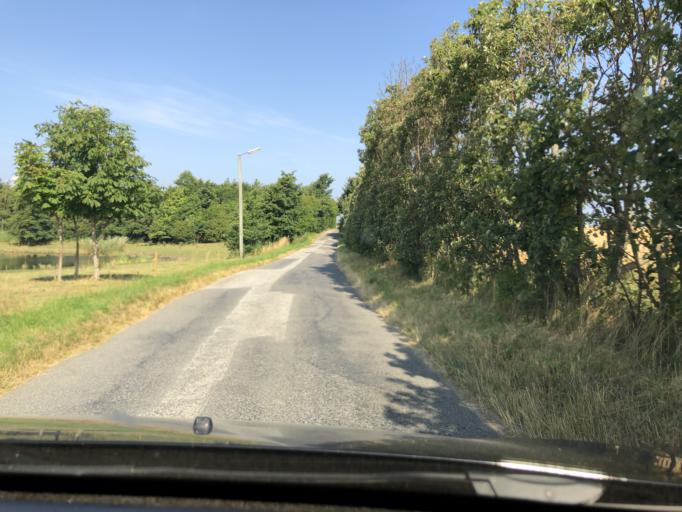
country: DK
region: South Denmark
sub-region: Faaborg-Midtfyn Kommune
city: Faaborg
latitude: 54.9418
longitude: 10.2499
